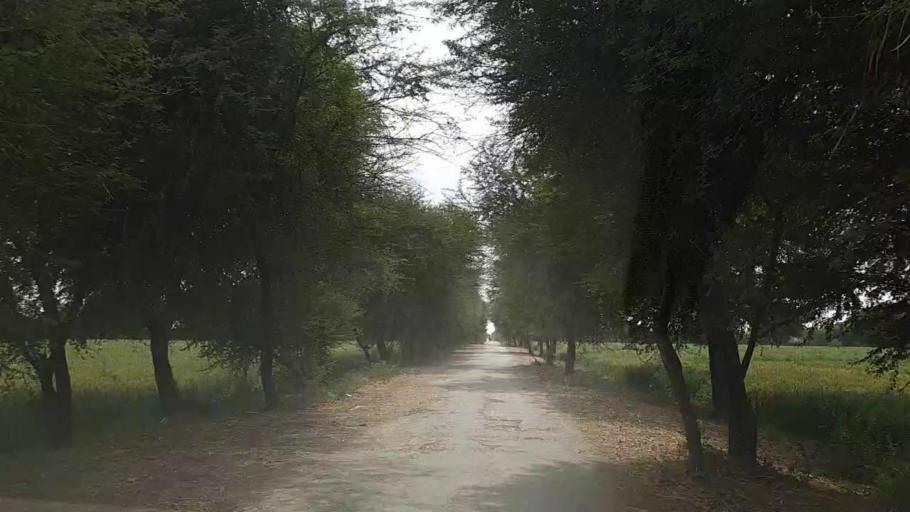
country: PK
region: Sindh
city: Samaro
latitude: 25.2811
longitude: 69.4537
